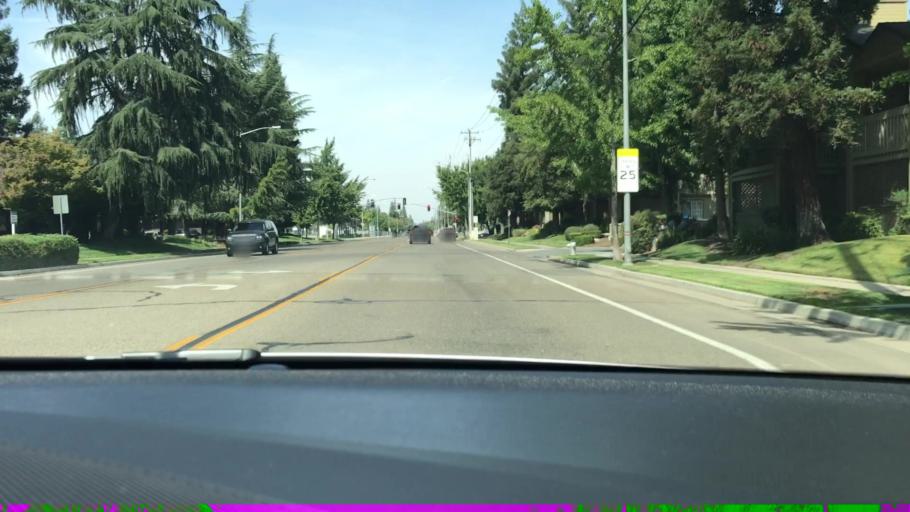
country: US
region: California
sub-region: Fresno County
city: Clovis
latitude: 36.8577
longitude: -119.7657
